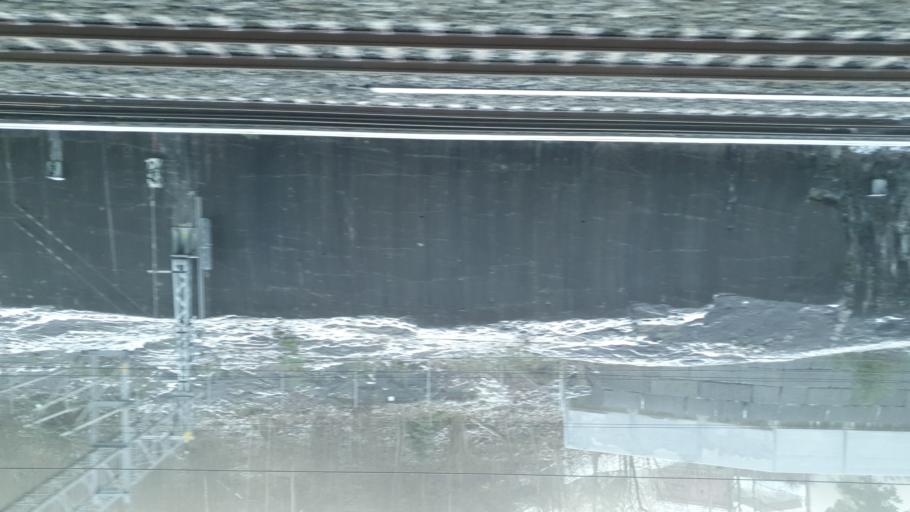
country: NO
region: Akershus
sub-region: Baerum
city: Sandvika
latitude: 59.8942
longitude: 10.5294
